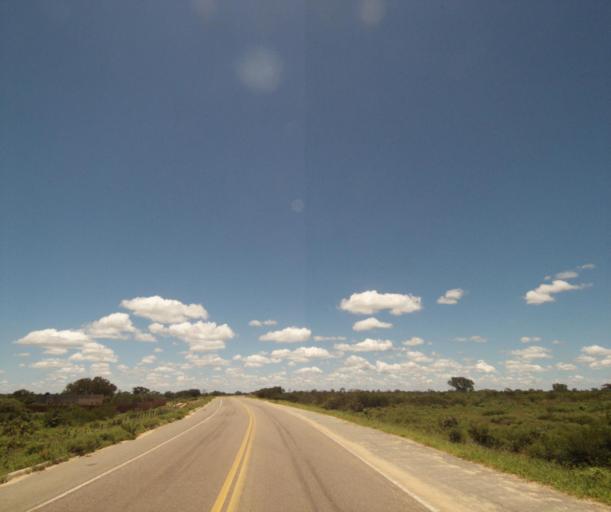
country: BR
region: Bahia
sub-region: Carinhanha
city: Carinhanha
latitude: -14.2900
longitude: -43.7794
